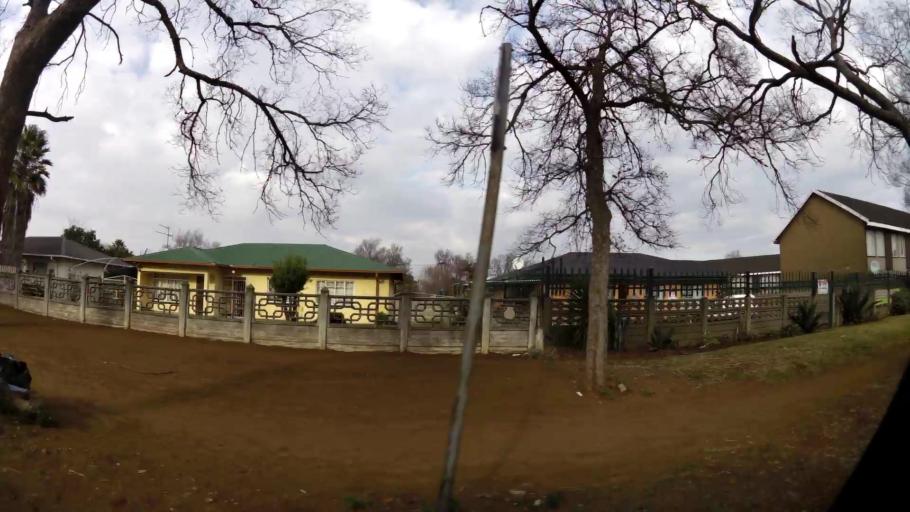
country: ZA
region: Gauteng
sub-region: Sedibeng District Municipality
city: Vanderbijlpark
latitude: -26.6922
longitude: 27.8140
